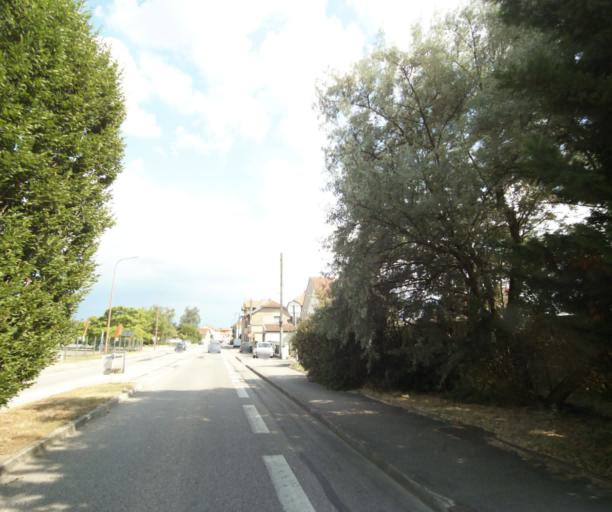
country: FR
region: Lorraine
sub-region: Departement de Meurthe-et-Moselle
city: Chanteheux
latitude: 48.5780
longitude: 6.5232
